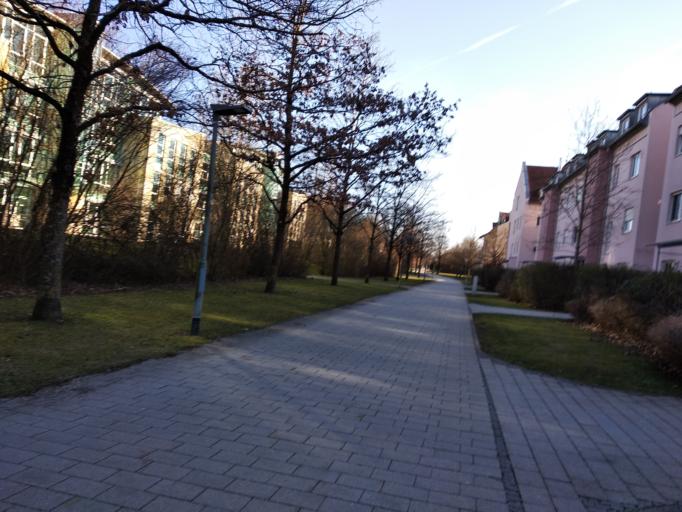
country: DE
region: Bavaria
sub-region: Upper Bavaria
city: Unterhaching
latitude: 48.0618
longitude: 11.6296
